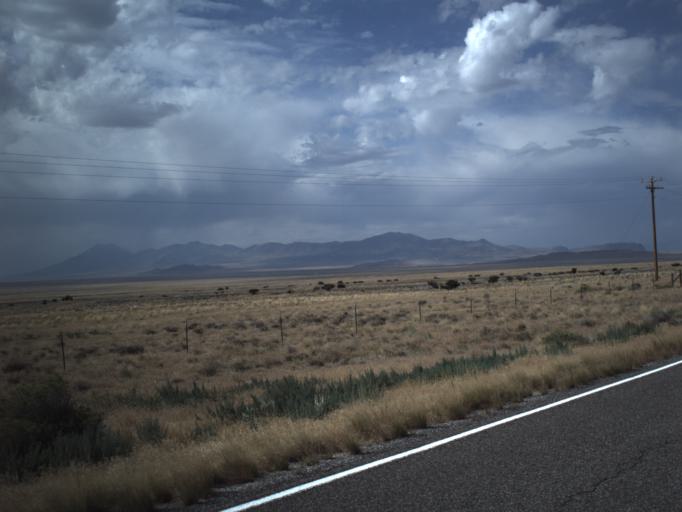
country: US
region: Utah
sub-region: Tooele County
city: Wendover
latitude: 41.4351
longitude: -113.7603
